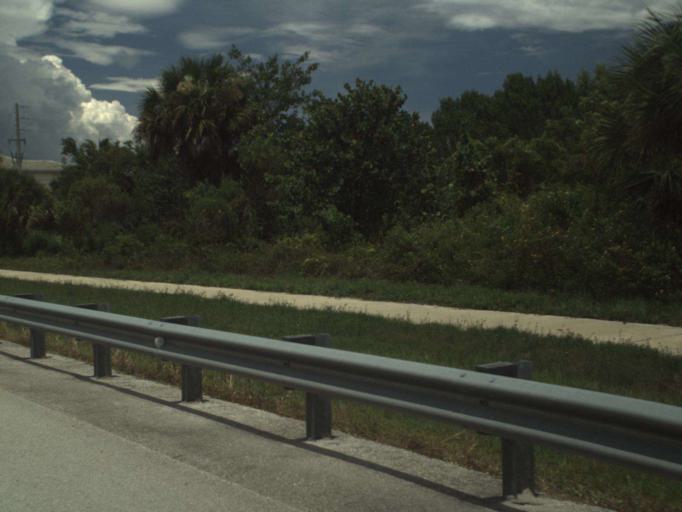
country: US
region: Florida
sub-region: Saint Lucie County
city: Fort Pierce
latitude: 27.4365
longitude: -80.2854
